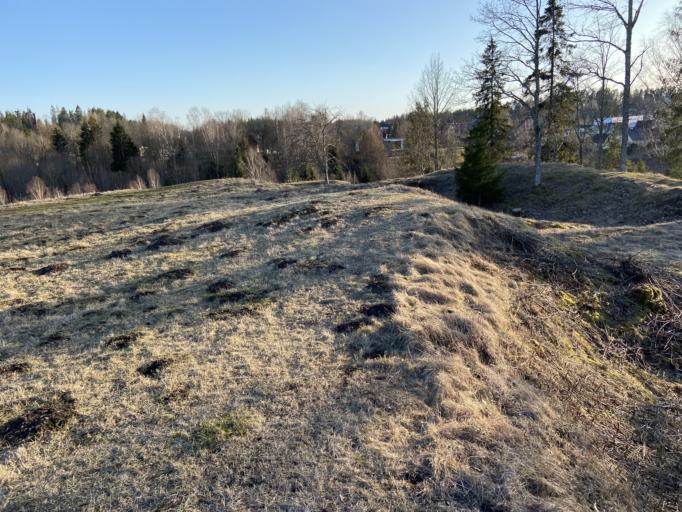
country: EE
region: Tartu
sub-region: Elva linn
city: Elva
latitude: 58.0571
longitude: 26.5037
